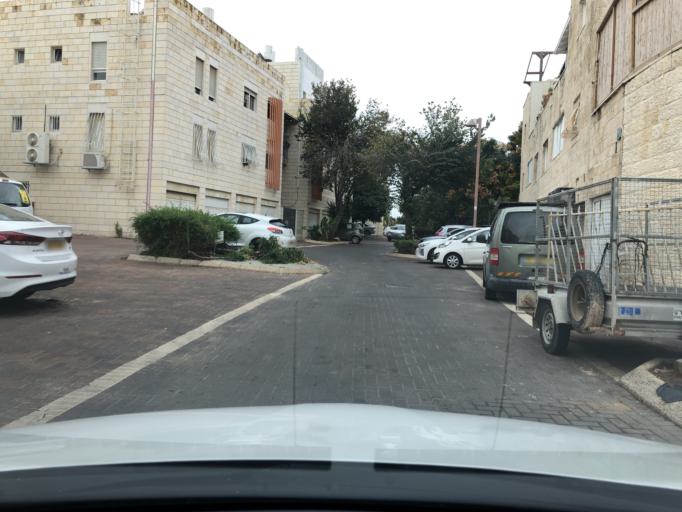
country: IL
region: Central District
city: Modiin
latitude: 31.9064
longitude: 35.0102
